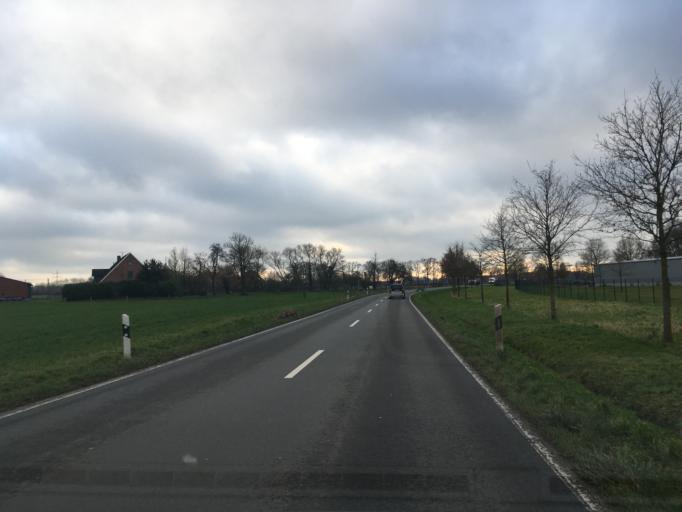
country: DE
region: North Rhine-Westphalia
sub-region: Regierungsbezirk Munster
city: Velen
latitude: 51.9415
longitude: 6.9551
